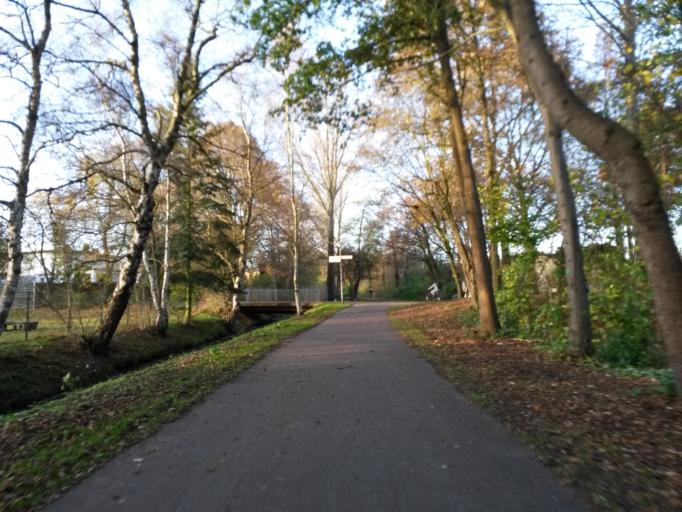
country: DE
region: Lower Saxony
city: Lilienthal
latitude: 53.0757
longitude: 8.9139
